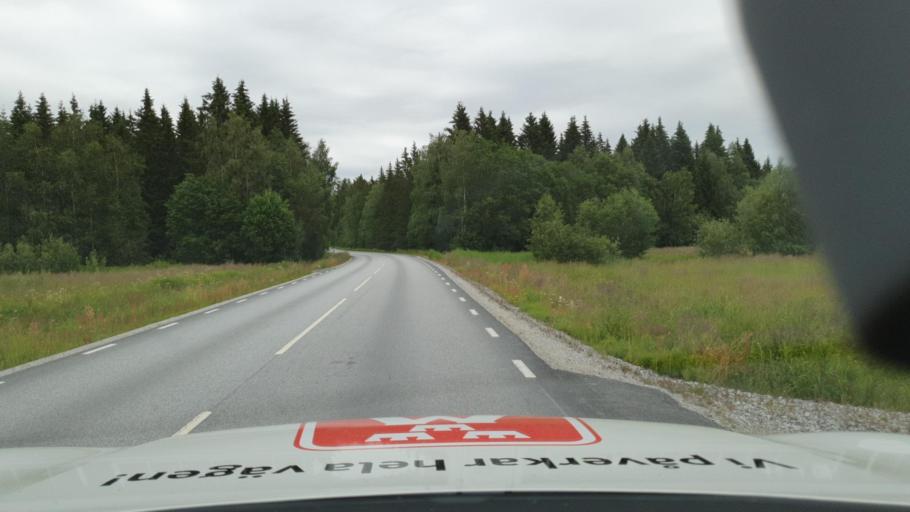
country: SE
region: Vaesterbotten
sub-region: Nordmalings Kommun
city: Nordmaling
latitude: 63.5659
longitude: 19.4188
